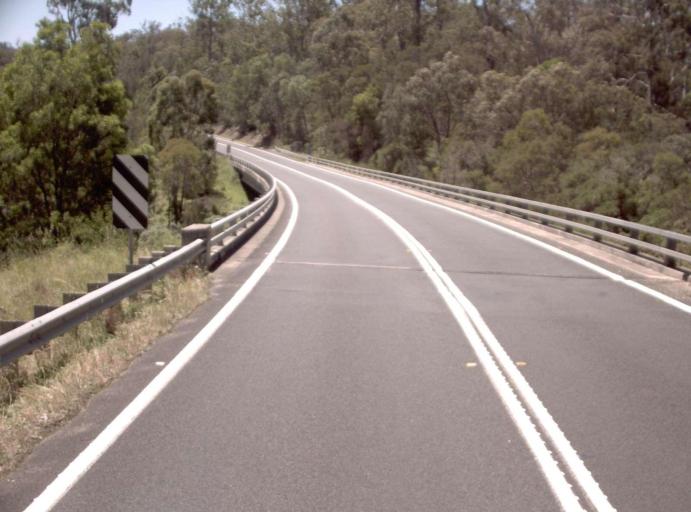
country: AU
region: Victoria
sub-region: East Gippsland
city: Lakes Entrance
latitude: -37.8026
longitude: 148.0464
